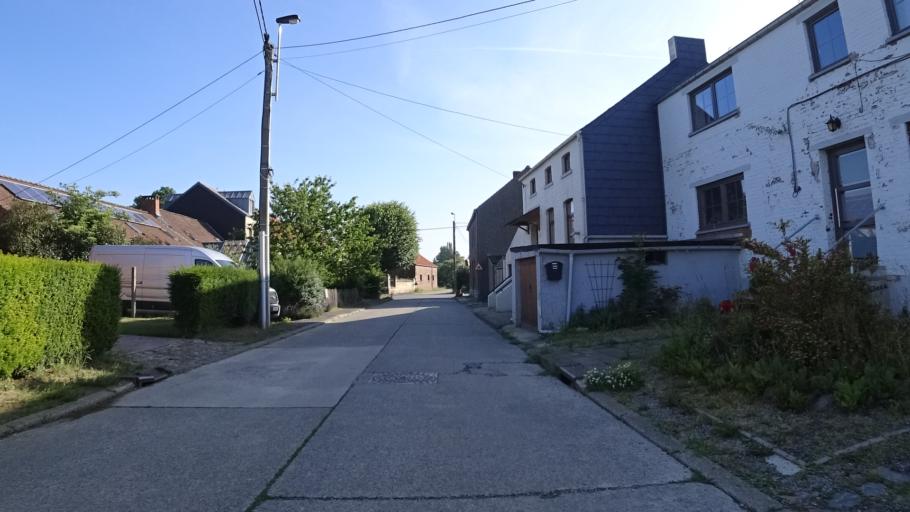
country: BE
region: Wallonia
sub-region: Province du Brabant Wallon
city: Walhain-Saint-Paul
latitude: 50.6123
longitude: 4.7208
